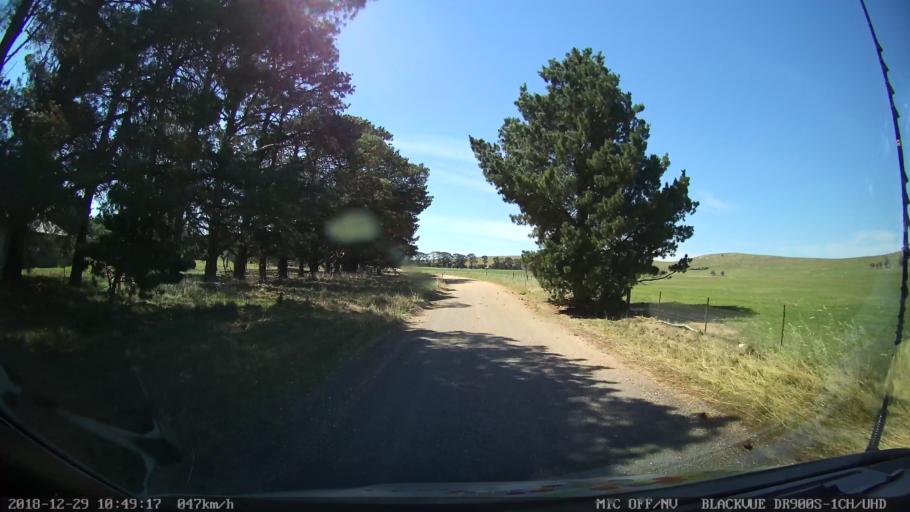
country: AU
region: New South Wales
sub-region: Palerang
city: Bungendore
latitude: -35.0745
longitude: 149.5150
